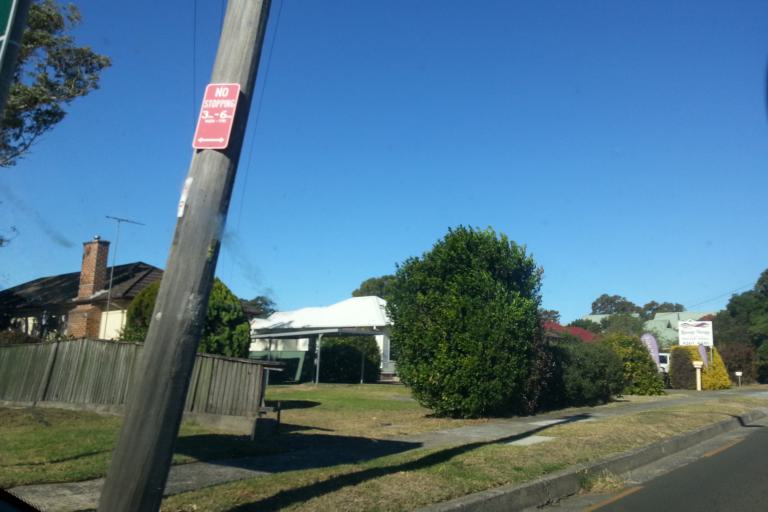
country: AU
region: New South Wales
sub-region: Wollongong
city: Dapto
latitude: -34.4970
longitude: 150.7922
